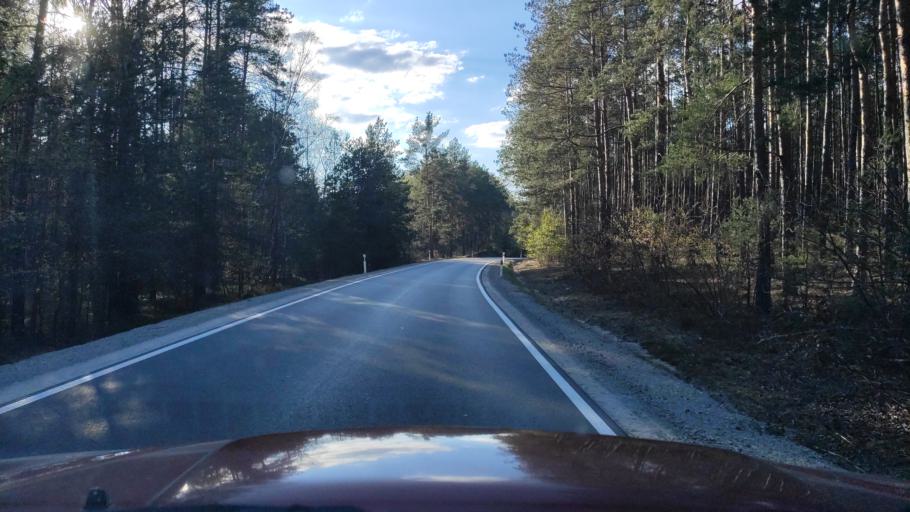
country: PL
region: Masovian Voivodeship
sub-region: Powiat zwolenski
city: Zwolen
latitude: 51.4084
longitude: 21.5210
